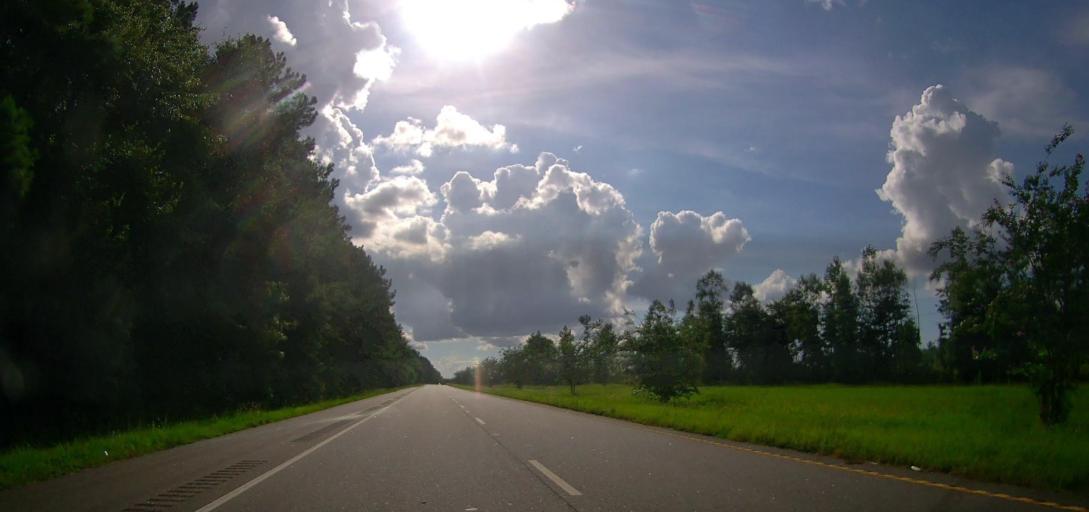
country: US
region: Georgia
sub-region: Talbot County
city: Talbotton
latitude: 32.5457
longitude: -84.7169
